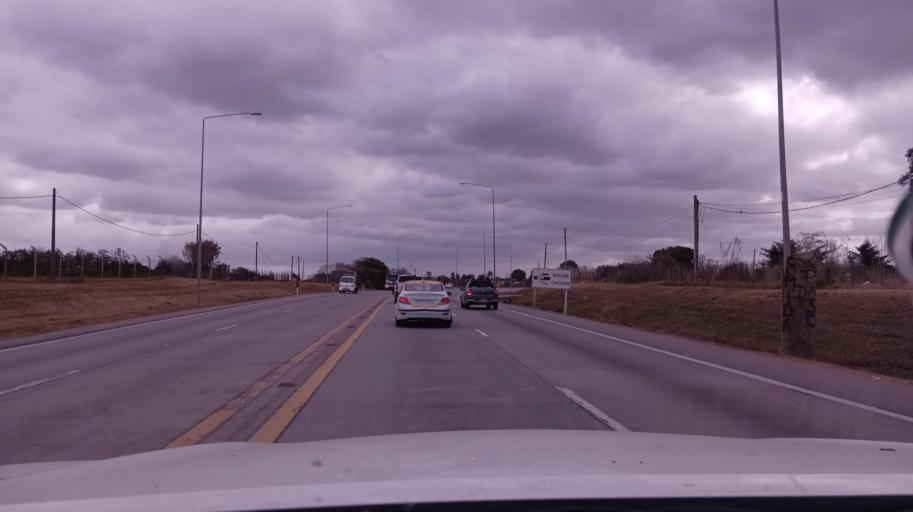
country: UY
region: Canelones
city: La Paz
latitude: -34.7978
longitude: -56.1565
